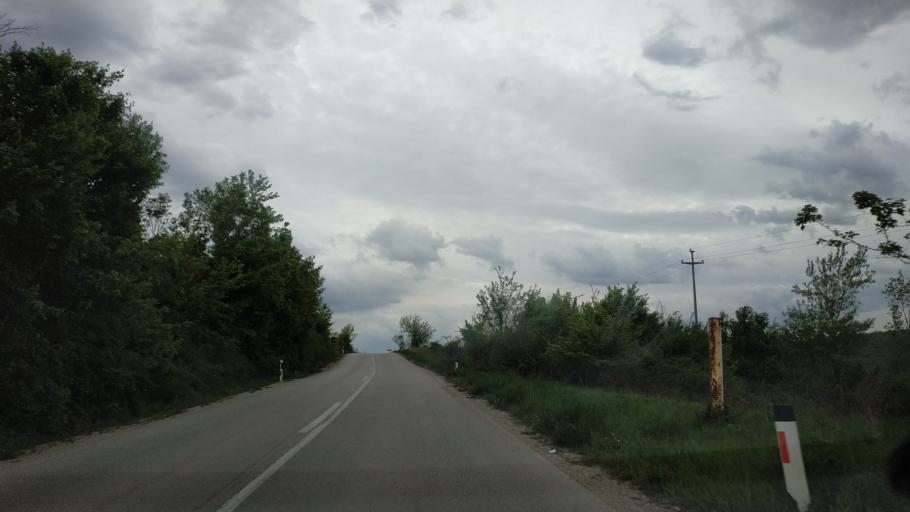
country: RS
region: Central Serbia
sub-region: Nisavski Okrug
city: Aleksinac
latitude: 43.6113
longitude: 21.6889
